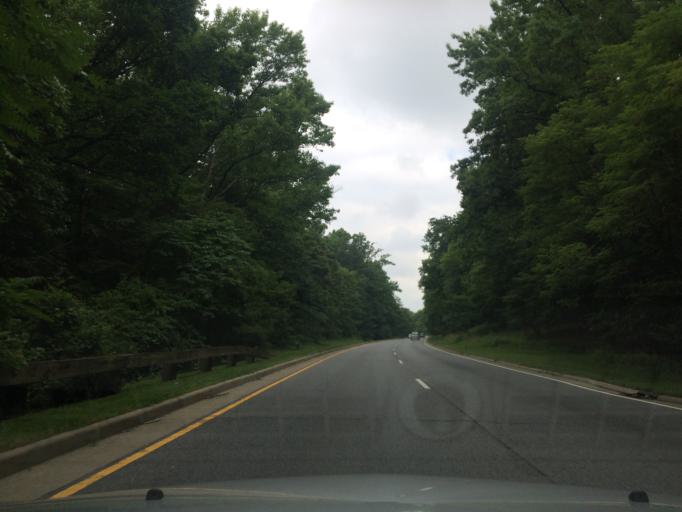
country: US
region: Maryland
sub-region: Prince George's County
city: Silver Hill
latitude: 38.8479
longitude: -76.9416
